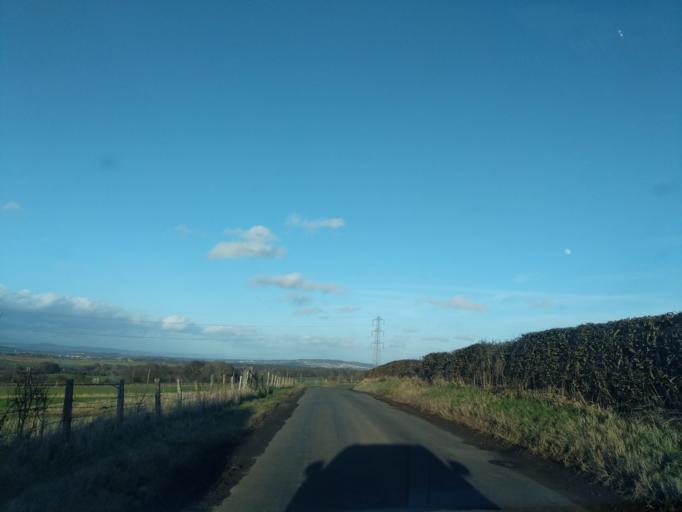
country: GB
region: Scotland
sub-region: West Lothian
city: Kirknewton
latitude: 55.8899
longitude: -3.4003
